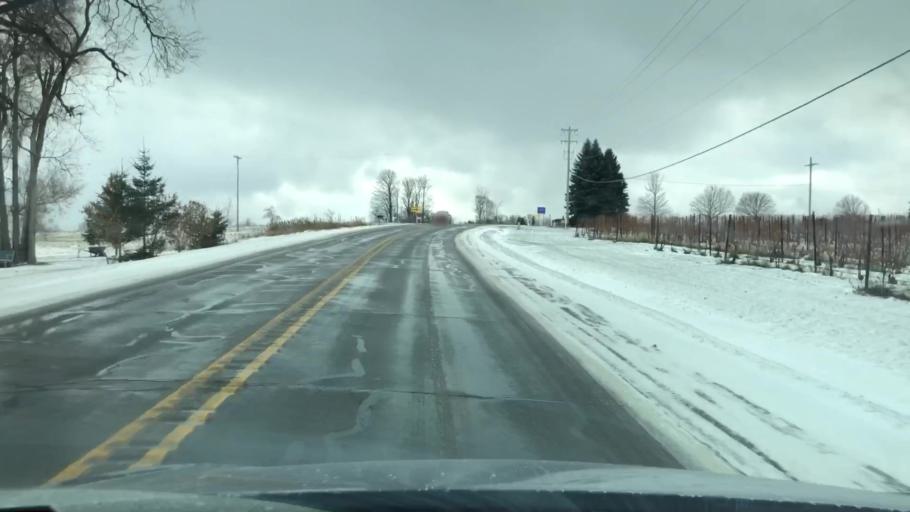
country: US
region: Michigan
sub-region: Antrim County
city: Elk Rapids
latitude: 44.8662
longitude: -85.5166
